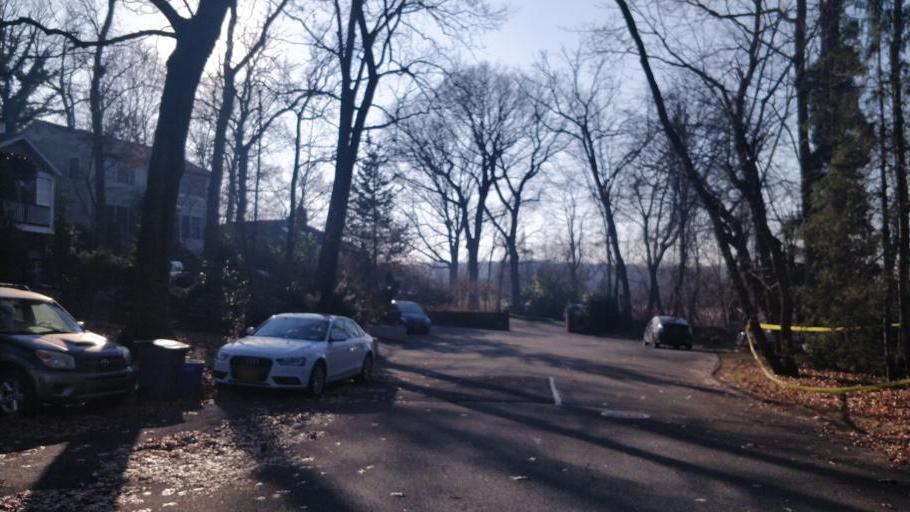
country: US
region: New York
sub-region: Nassau County
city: Bayville
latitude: 40.9068
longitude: -73.5776
